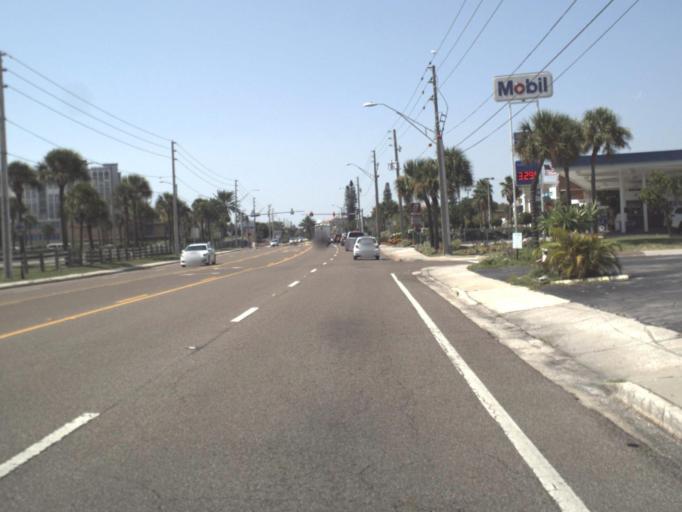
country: US
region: Florida
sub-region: Pinellas County
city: Saint Pete Beach
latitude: 27.7203
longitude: -82.7397
